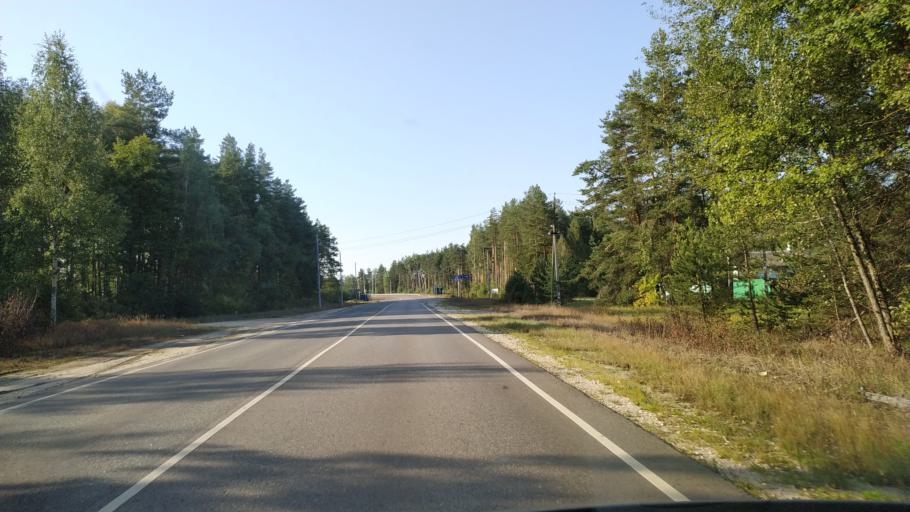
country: RU
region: Moskovskaya
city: Tugolesskiy Bor
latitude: 55.4358
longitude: 39.7217
